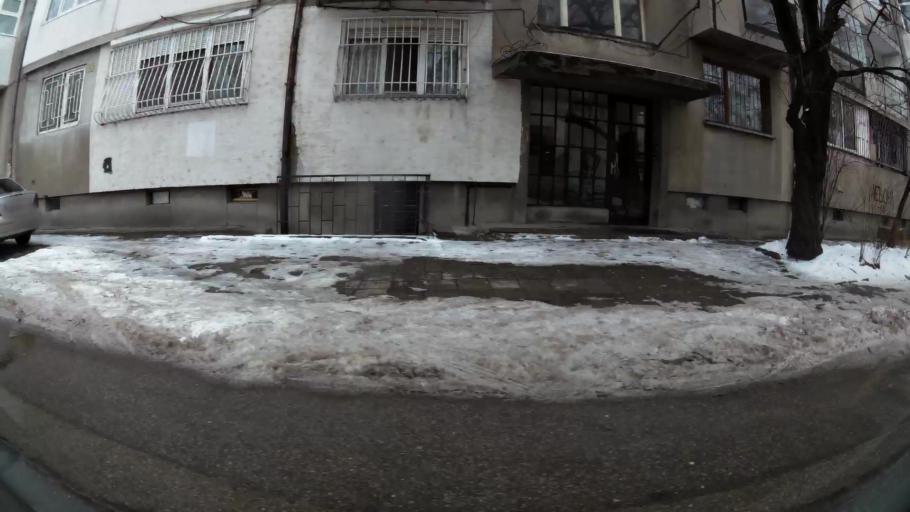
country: BG
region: Sofia-Capital
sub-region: Stolichna Obshtina
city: Sofia
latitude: 42.7006
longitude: 23.3643
